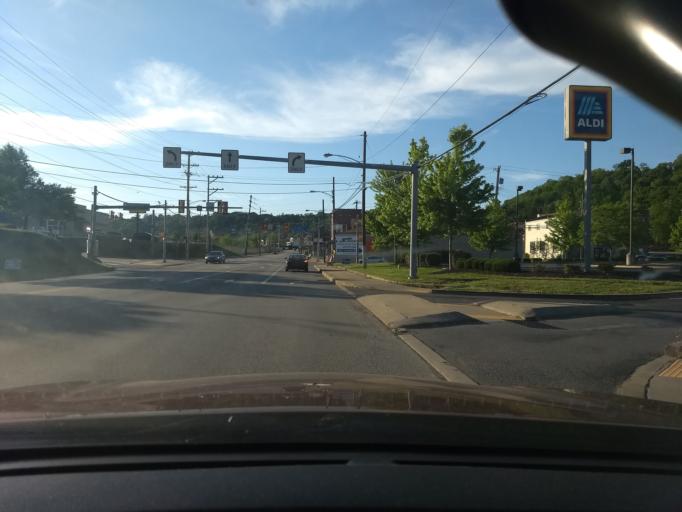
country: US
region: Pennsylvania
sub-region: Allegheny County
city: Versailles
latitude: 40.3268
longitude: -79.8398
